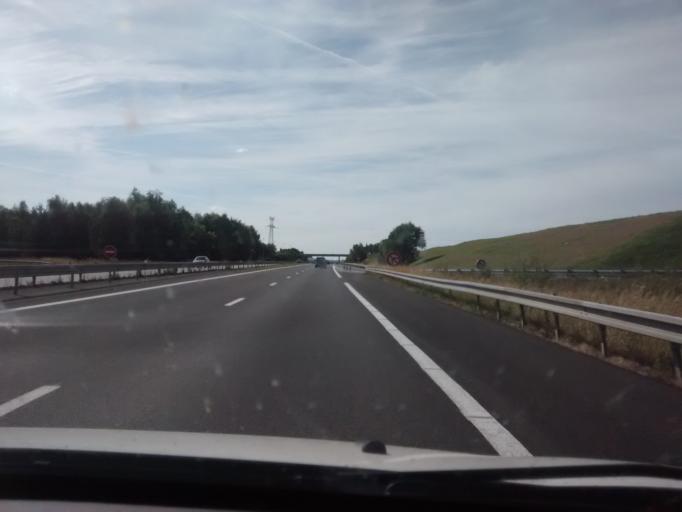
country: FR
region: Pays de la Loire
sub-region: Departement de la Mayenne
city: Louverne
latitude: 48.1052
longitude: -0.7375
